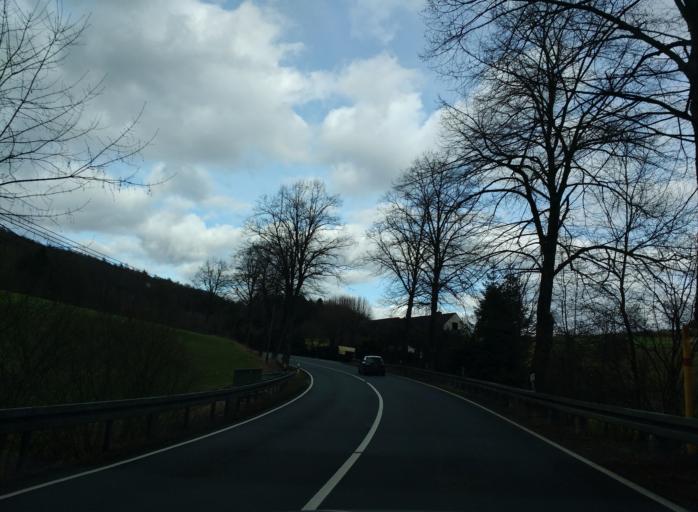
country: DE
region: North Rhine-Westphalia
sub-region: Regierungsbezirk Detmold
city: Lemgo
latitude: 52.0687
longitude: 8.9167
